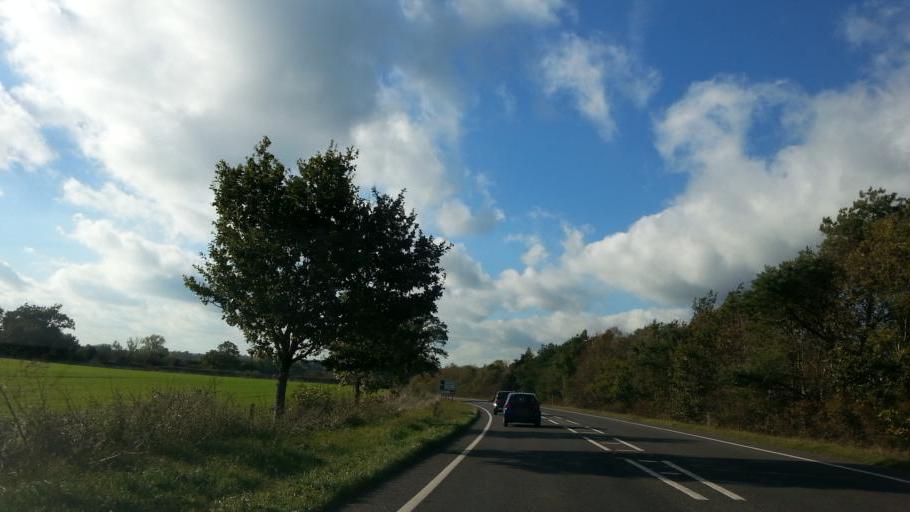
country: GB
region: England
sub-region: Norfolk
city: Loddon
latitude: 52.4857
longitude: 1.4981
